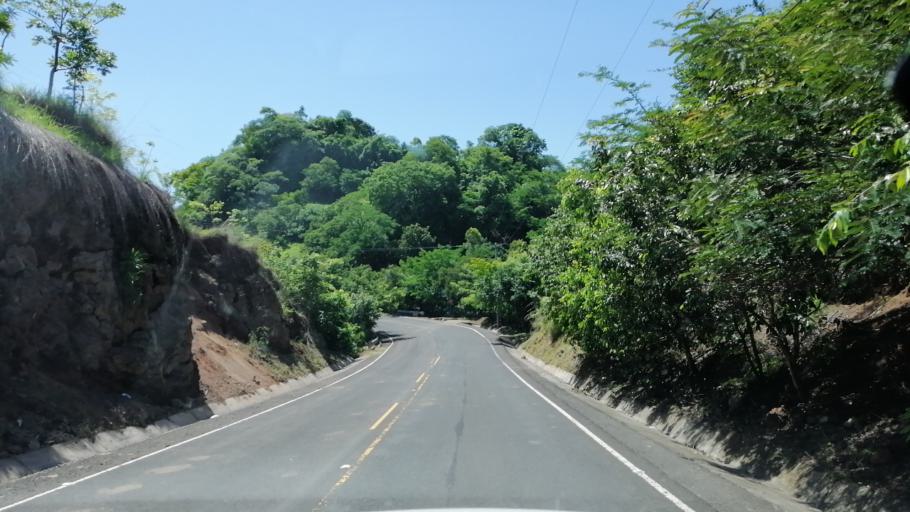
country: SV
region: San Miguel
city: Sesori
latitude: 13.8050
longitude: -88.3836
